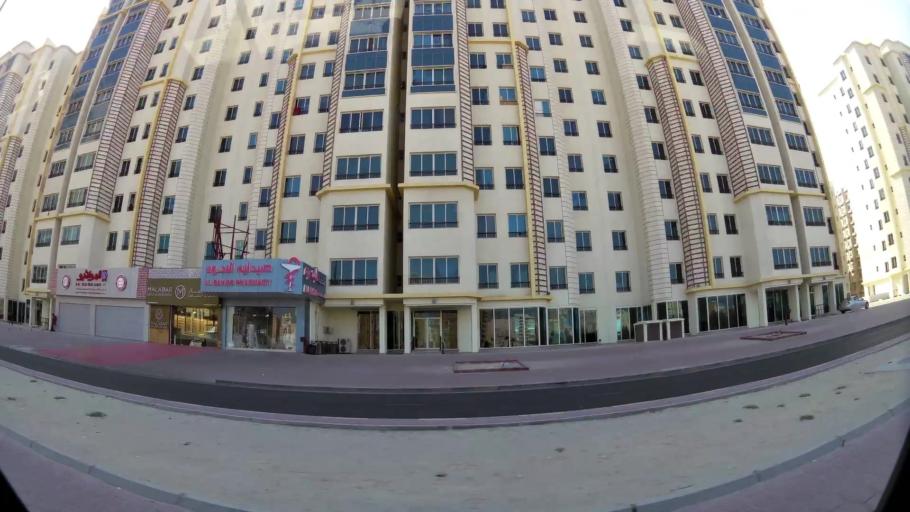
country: KW
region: Al Ahmadi
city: Al Mahbulah
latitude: 29.1509
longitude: 48.1181
